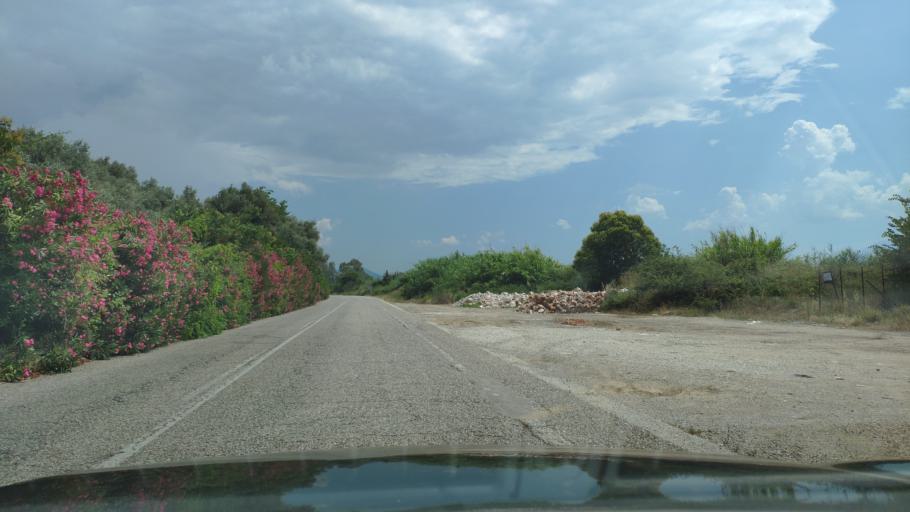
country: GR
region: West Greece
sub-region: Nomos Aitolias kai Akarnanias
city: Krikellos
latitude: 38.9843
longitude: 21.1621
